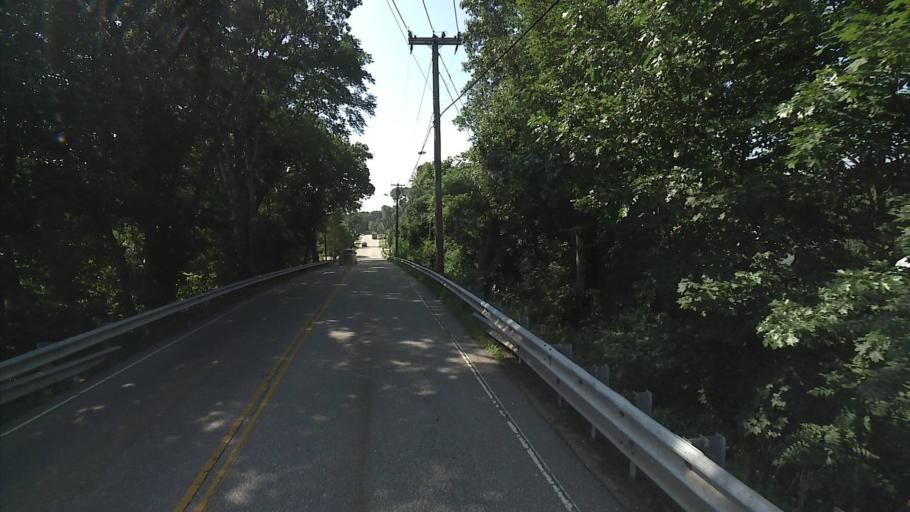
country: US
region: Connecticut
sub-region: Middlesex County
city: Clinton
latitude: 41.2776
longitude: -72.4853
